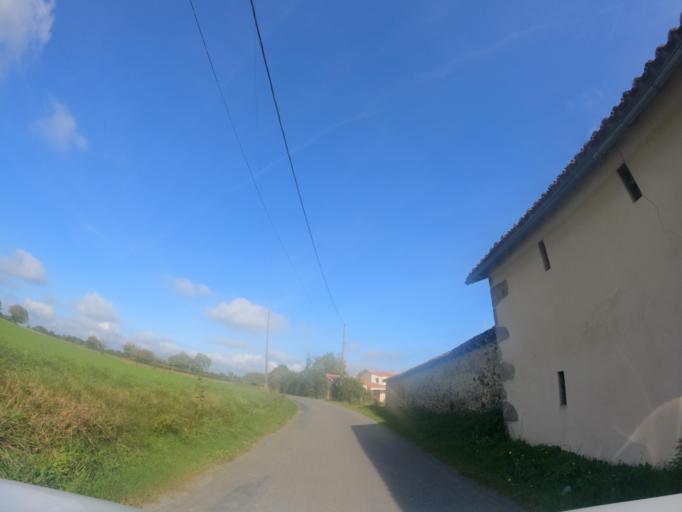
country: FR
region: Poitou-Charentes
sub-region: Departement des Deux-Sevres
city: Courlay
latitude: 46.7848
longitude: -0.5899
